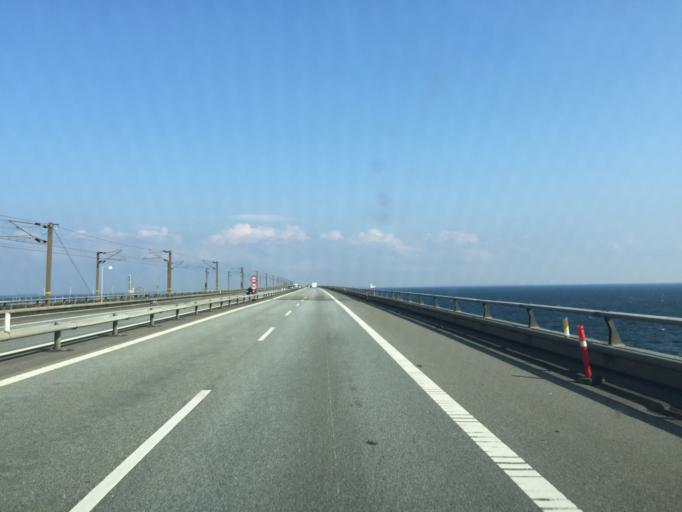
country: DK
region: South Denmark
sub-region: Nyborg Kommune
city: Nyborg
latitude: 55.3022
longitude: 10.8684
